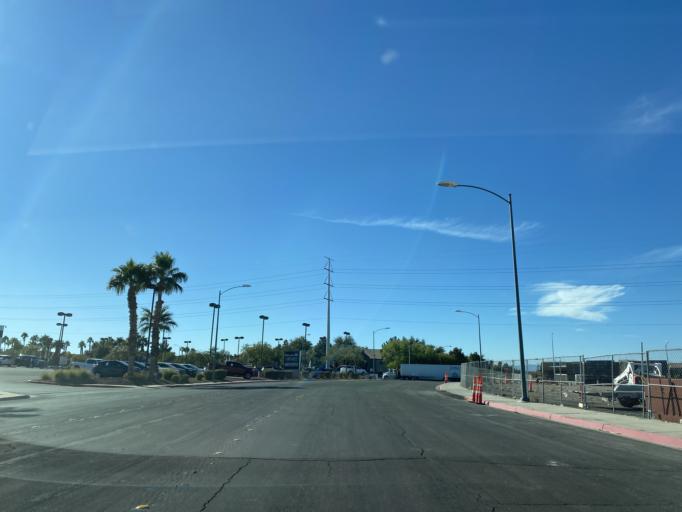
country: US
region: Nevada
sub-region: Clark County
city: Henderson
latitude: 36.0530
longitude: -115.0275
